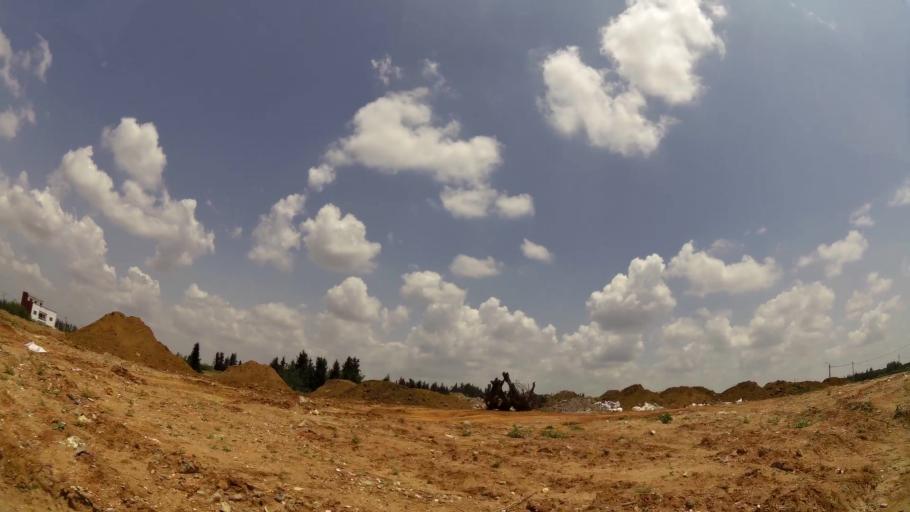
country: MA
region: Rabat-Sale-Zemmour-Zaer
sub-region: Khemisset
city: Tiflet
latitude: 34.0140
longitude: -6.5218
